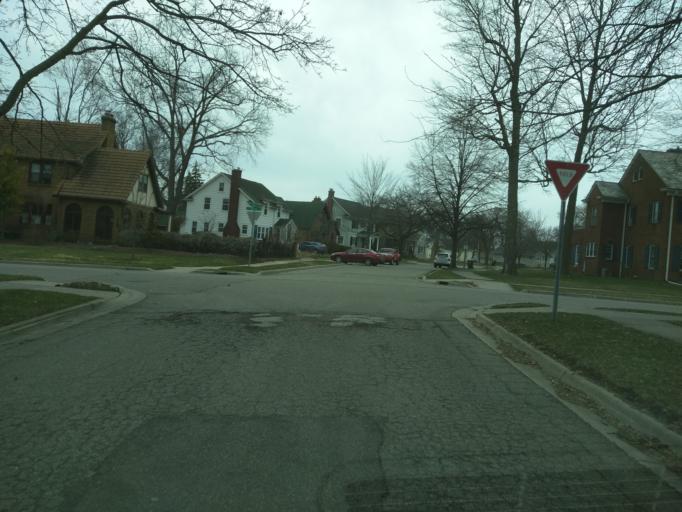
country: US
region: Michigan
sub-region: Ingham County
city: Lansing
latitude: 42.7384
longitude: -84.5739
